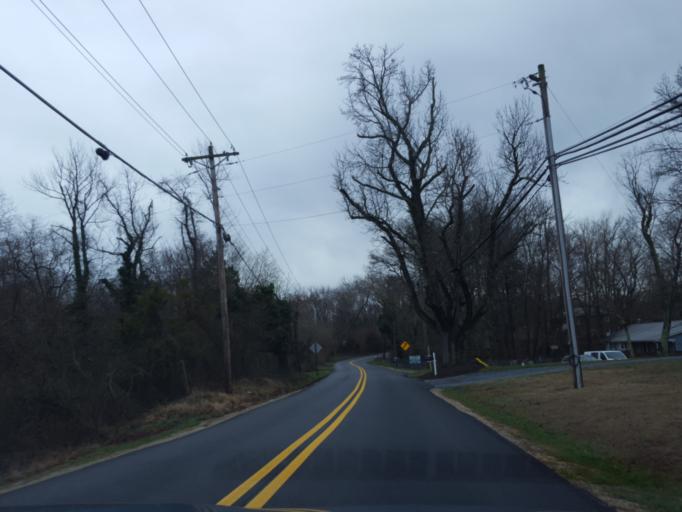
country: US
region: Maryland
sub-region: Calvert County
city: Owings
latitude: 38.6974
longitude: -76.6036
